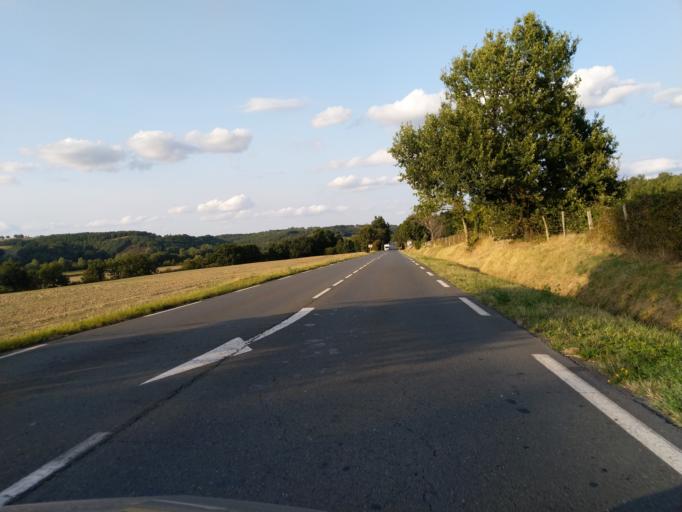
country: FR
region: Midi-Pyrenees
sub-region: Departement du Tarn
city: Realmont
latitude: 43.8201
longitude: 2.1819
